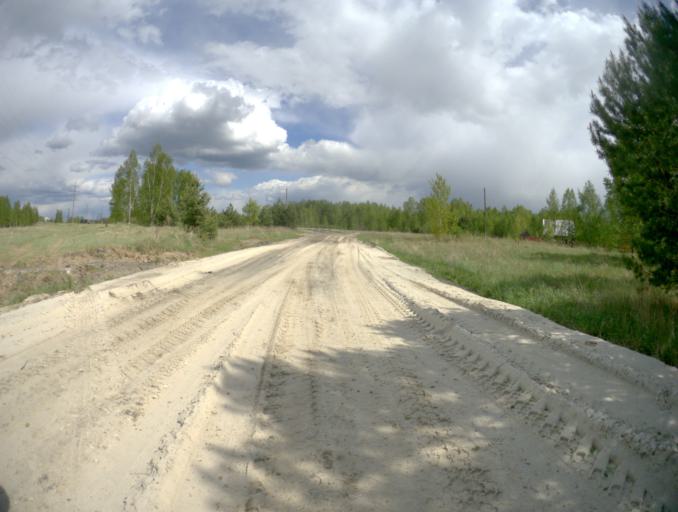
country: RU
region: Vladimir
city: Velikodvorskiy
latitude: 55.2275
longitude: 40.6435
